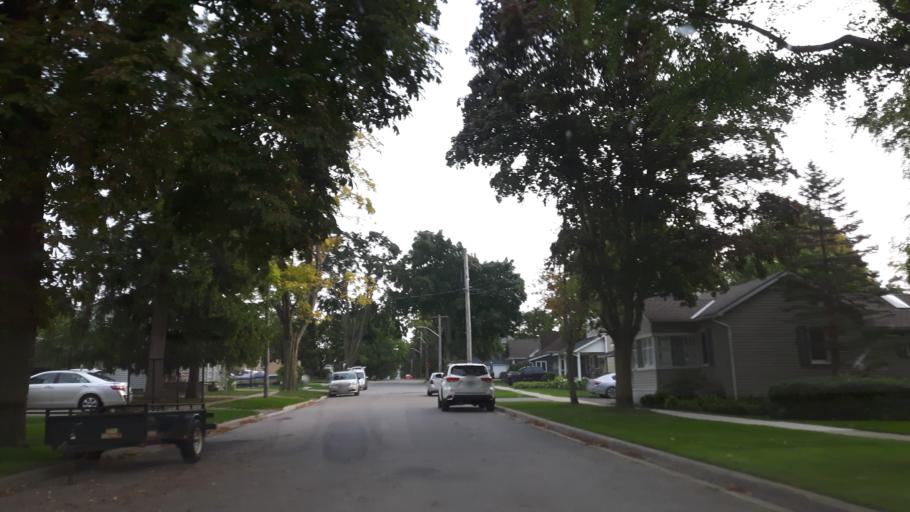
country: CA
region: Ontario
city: Goderich
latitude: 43.7384
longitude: -81.7099
